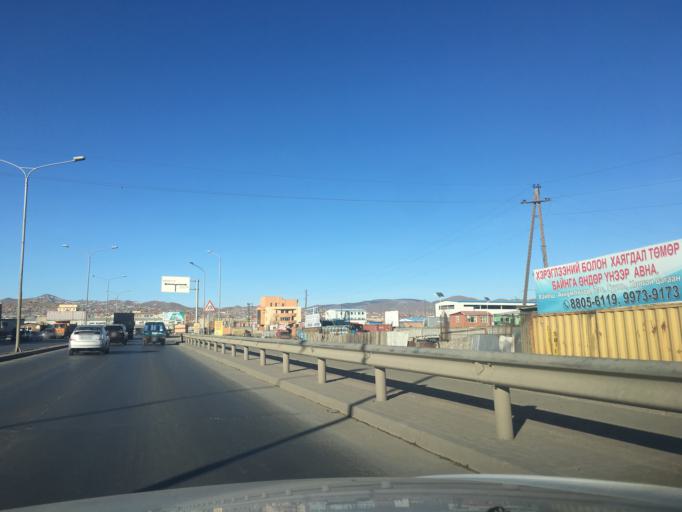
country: MN
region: Ulaanbaatar
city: Ulaanbaatar
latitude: 47.9042
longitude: 106.7860
